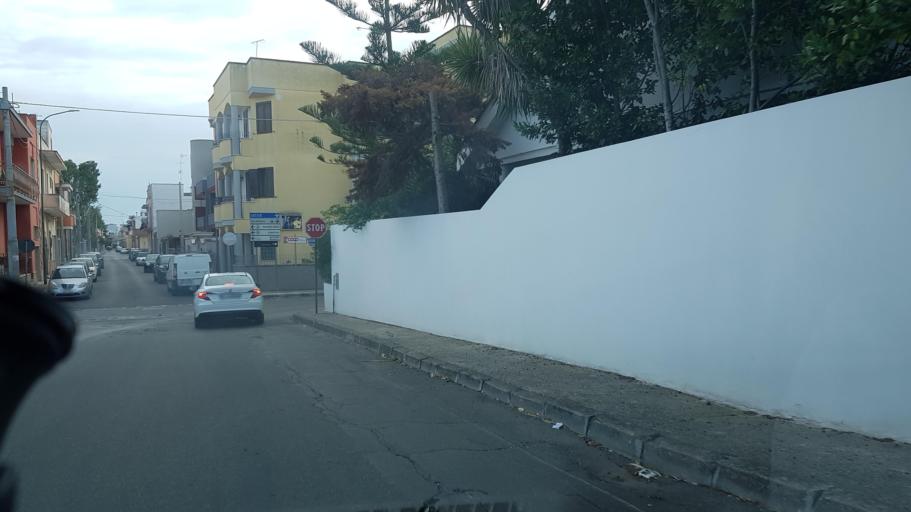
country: IT
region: Apulia
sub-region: Provincia di Lecce
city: Trepuzzi
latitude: 40.4111
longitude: 18.0729
